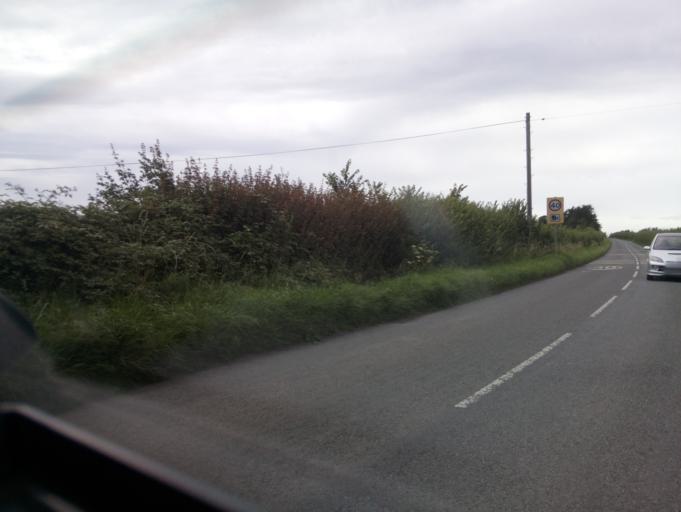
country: GB
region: England
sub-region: Somerset
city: Street
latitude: 51.1154
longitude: -2.7075
